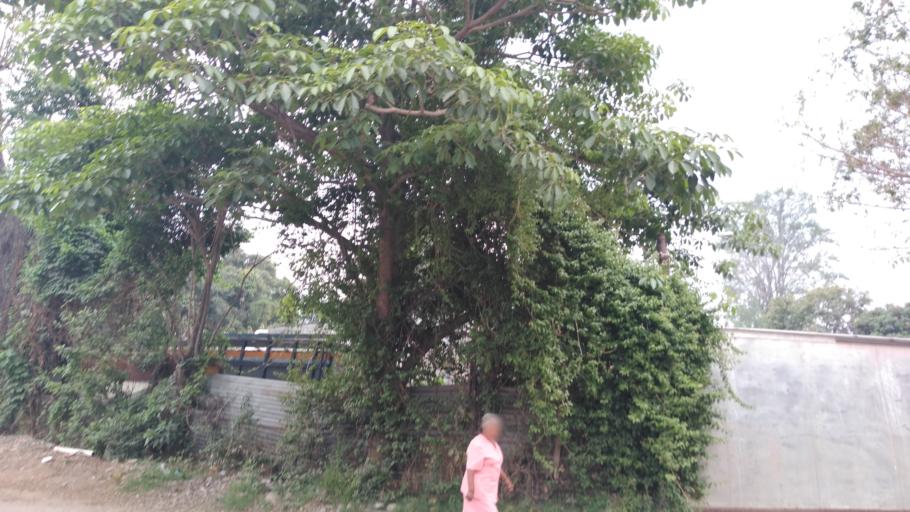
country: GT
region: Guatemala
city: Petapa
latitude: 14.5120
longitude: -90.5569
